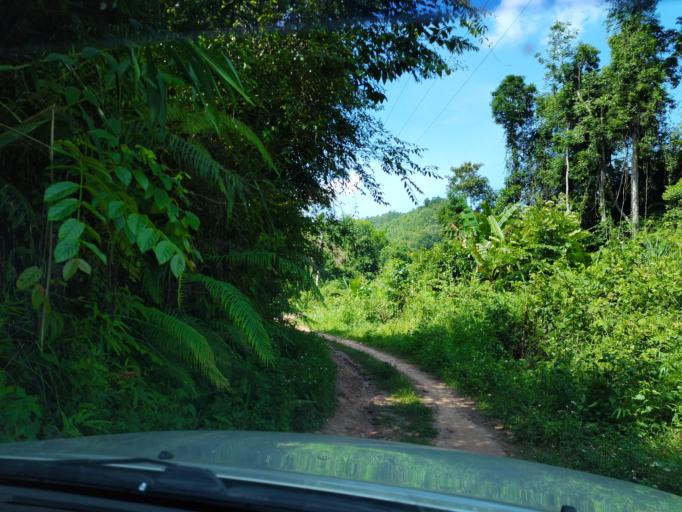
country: LA
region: Loungnamtha
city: Muang Nale
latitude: 20.5472
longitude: 101.0638
